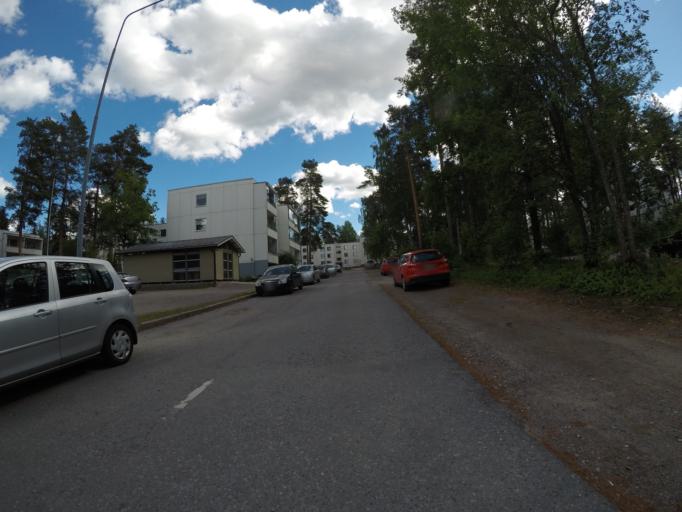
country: FI
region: Haeme
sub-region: Haemeenlinna
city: Haemeenlinna
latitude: 61.0150
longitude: 24.4359
